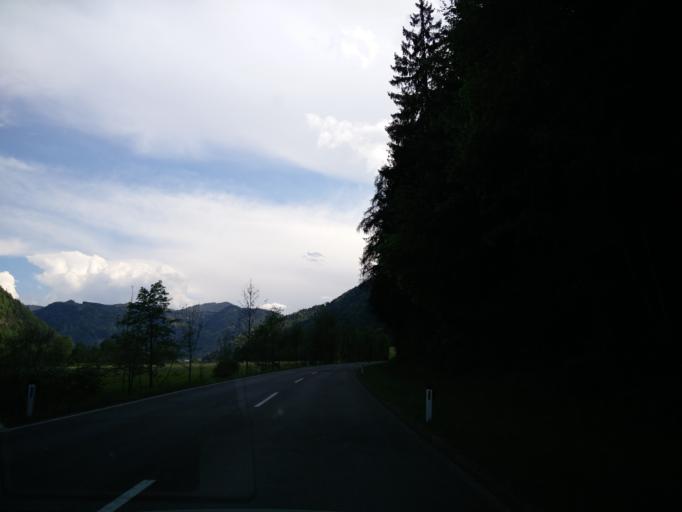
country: AT
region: Tyrol
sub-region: Politischer Bezirk Kitzbuhel
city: Kirchdorf in Tirol
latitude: 47.6072
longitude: 12.4679
